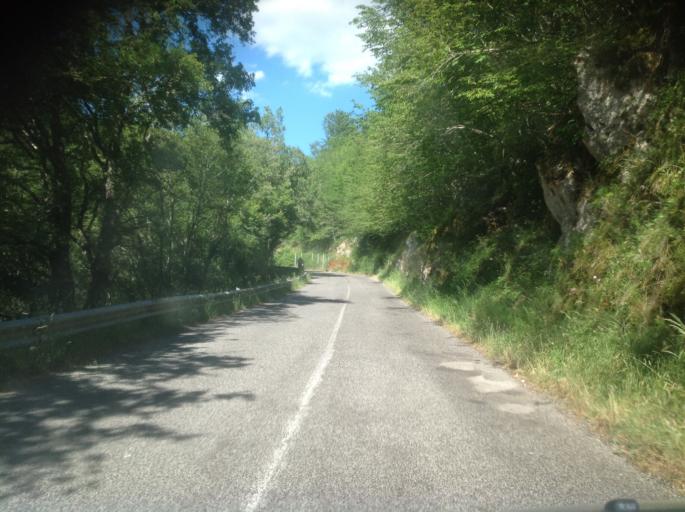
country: IT
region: Umbria
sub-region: Provincia di Terni
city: Stroncone
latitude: 42.4828
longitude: 12.7014
